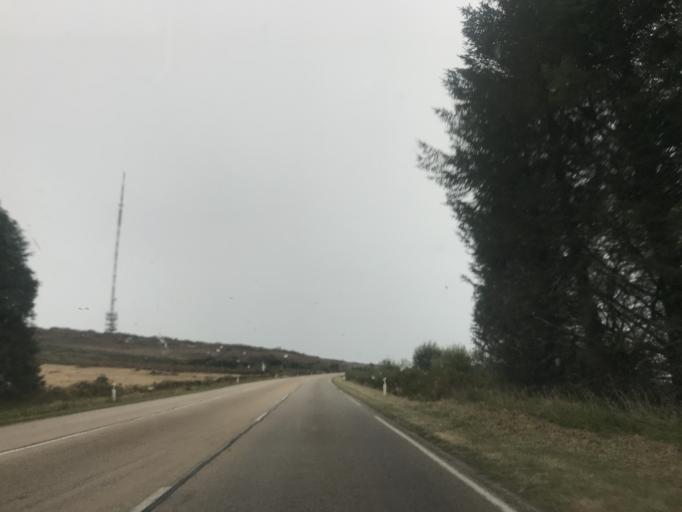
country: FR
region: Brittany
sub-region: Departement du Finistere
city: Plouneour-Menez
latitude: 48.4196
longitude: -3.8877
